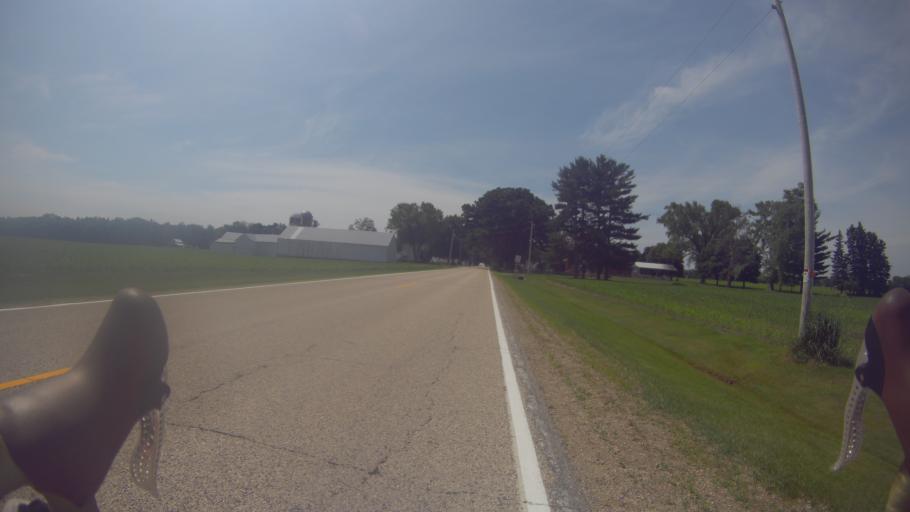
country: US
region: Wisconsin
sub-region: Jefferson County
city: Cambridge
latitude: 43.0516
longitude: -89.0115
